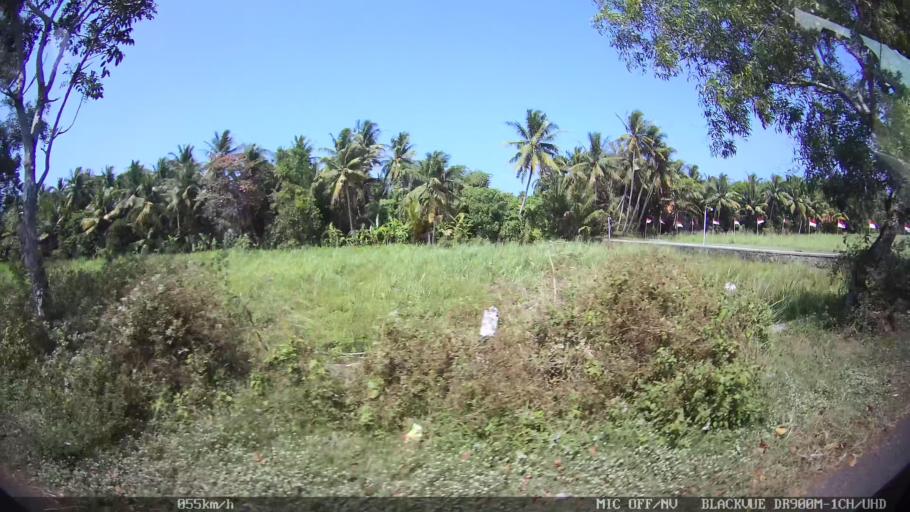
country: ID
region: Daerah Istimewa Yogyakarta
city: Srandakan
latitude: -7.9427
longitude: 110.1667
